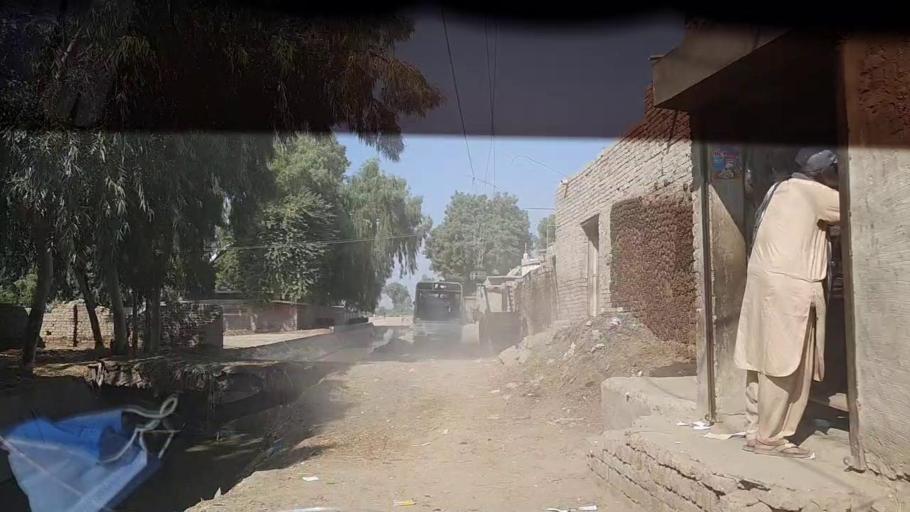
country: PK
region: Sindh
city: Naudero
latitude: 27.6617
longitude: 68.3745
